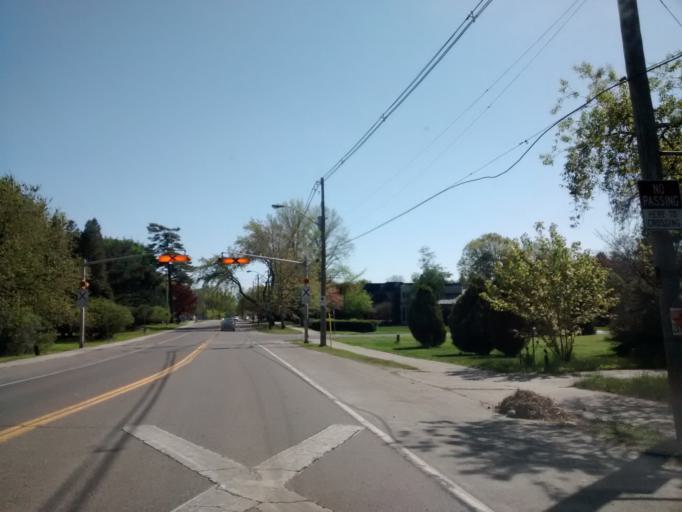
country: CA
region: Ontario
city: Oakville
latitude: 43.4086
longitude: -79.6934
